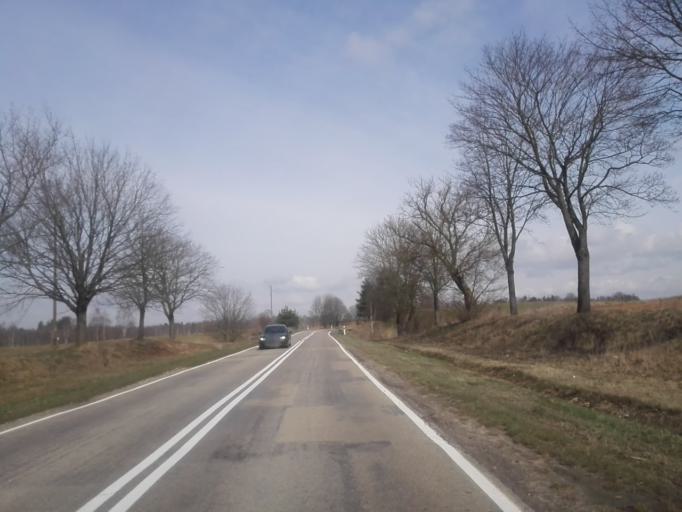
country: PL
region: Podlasie
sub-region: Powiat sejnenski
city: Sejny
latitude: 54.0527
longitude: 23.3550
